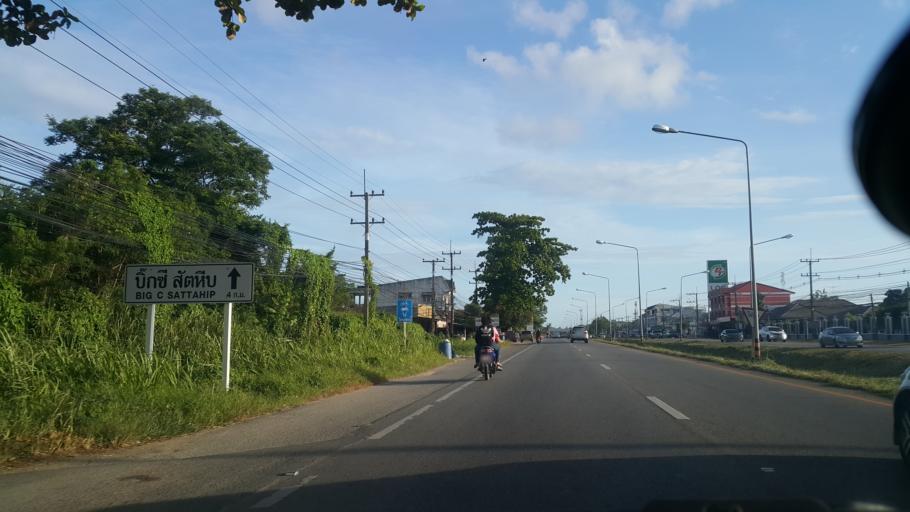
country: TH
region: Chon Buri
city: Sattahip
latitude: 12.7377
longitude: 100.8941
